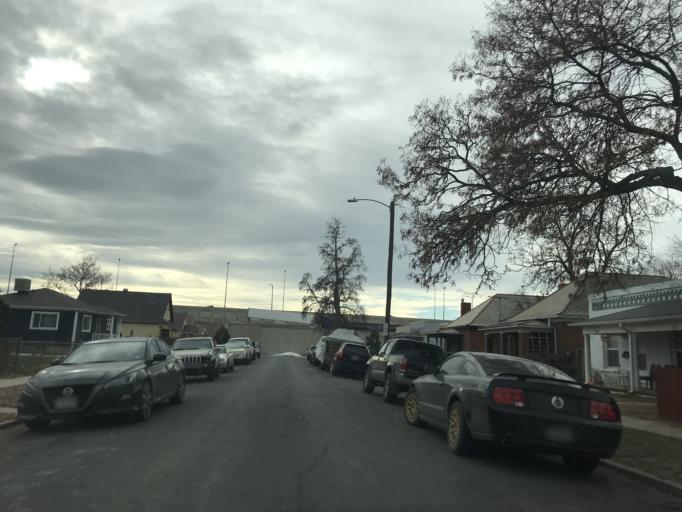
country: US
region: Colorado
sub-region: Adams County
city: Commerce City
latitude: 39.7816
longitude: -104.9656
